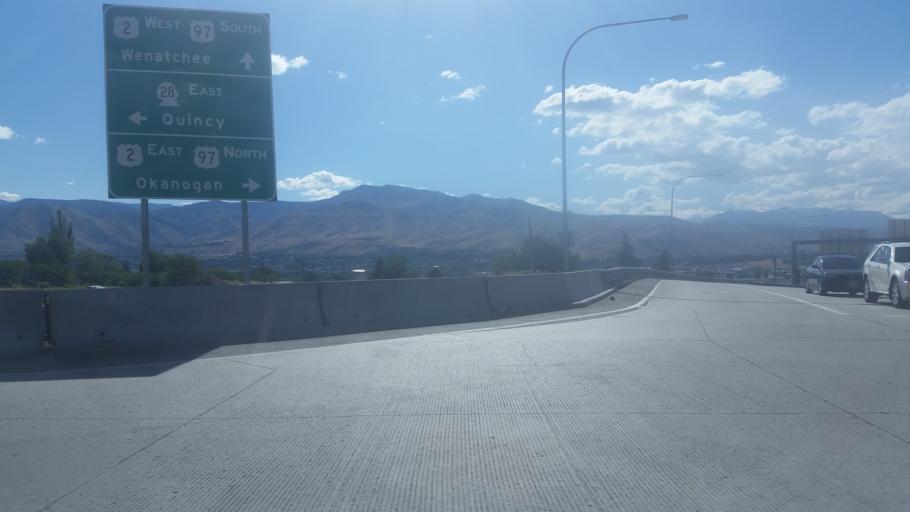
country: US
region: Washington
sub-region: Chelan County
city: Sunnyslope
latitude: 47.4677
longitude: -120.2996
